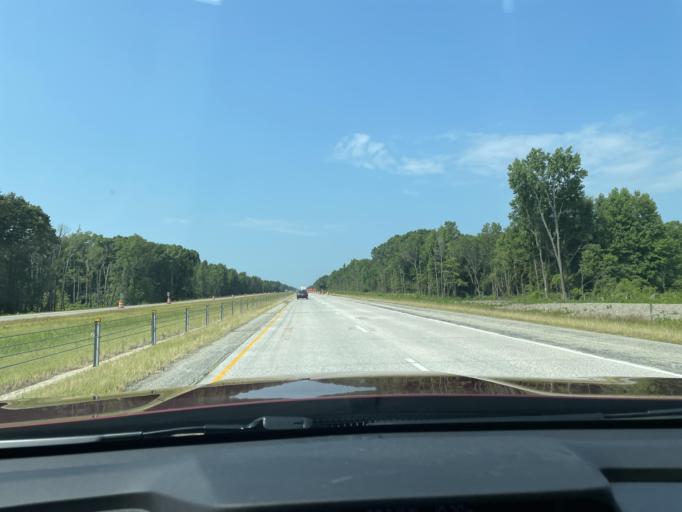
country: US
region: Arkansas
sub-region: White County
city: Searcy
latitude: 35.1852
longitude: -91.7537
